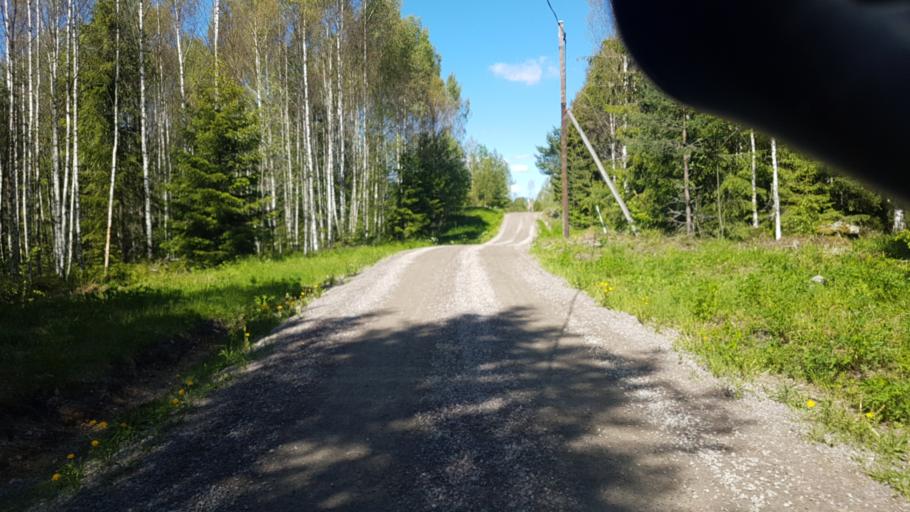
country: SE
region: Vaermland
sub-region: Arvika Kommun
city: Arvika
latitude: 59.5431
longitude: 12.8561
